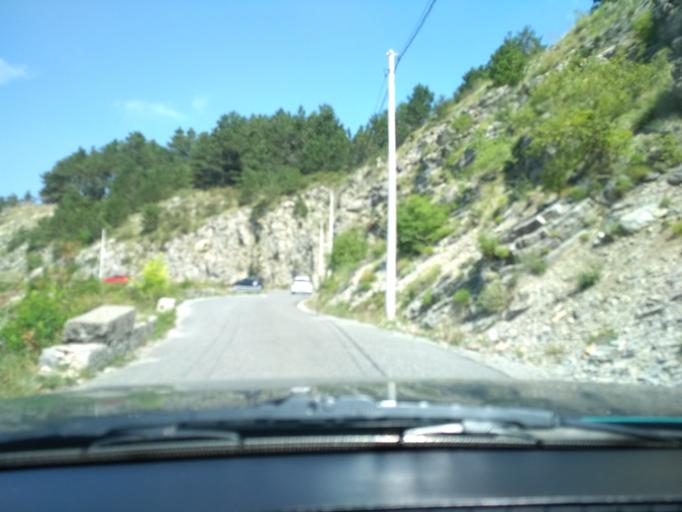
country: ME
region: Kotor
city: Kotor
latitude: 42.4234
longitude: 18.8008
